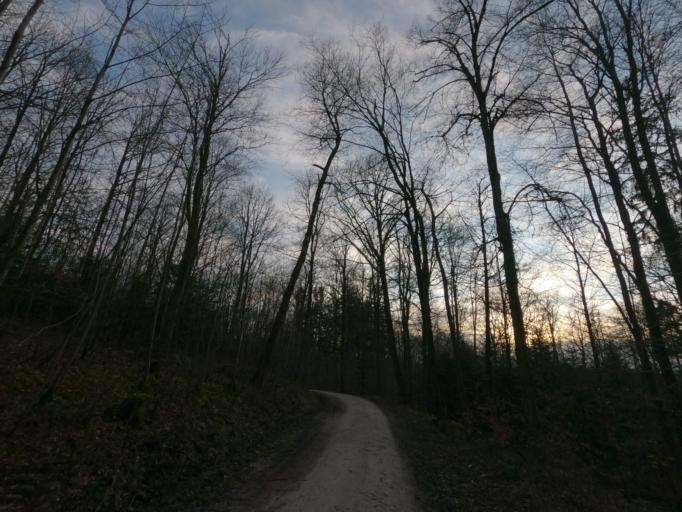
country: DE
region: Baden-Wuerttemberg
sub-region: Regierungsbezirk Stuttgart
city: Eislingen
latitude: 48.7270
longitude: 9.7096
